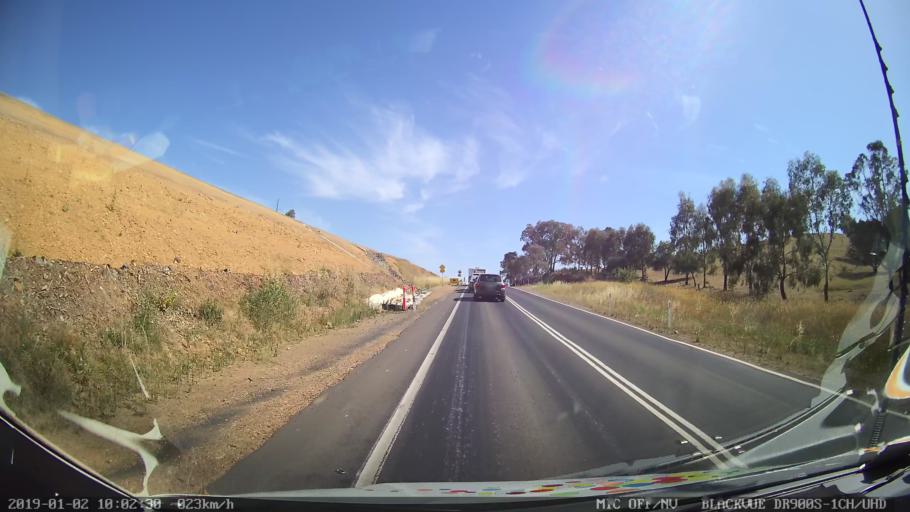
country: AU
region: New South Wales
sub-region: Gundagai
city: Gundagai
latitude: -35.1828
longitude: 148.1263
